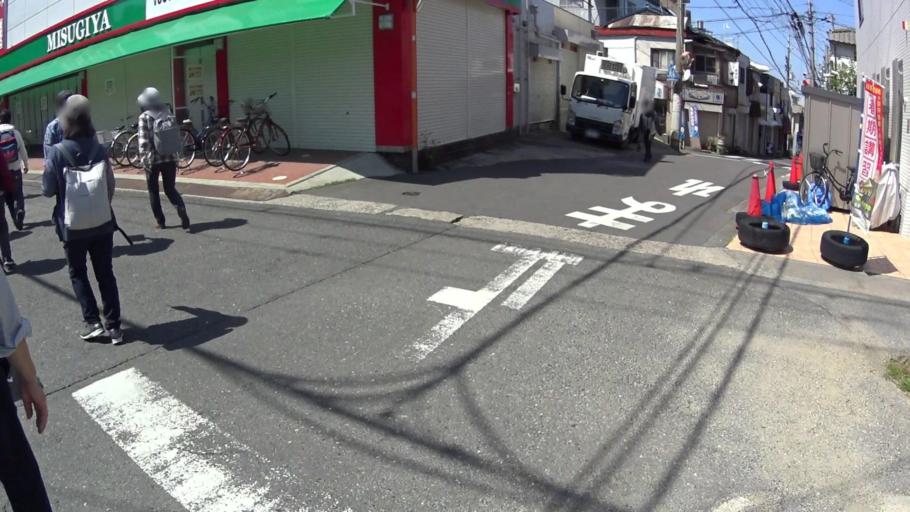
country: JP
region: Osaka
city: Kashihara
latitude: 34.5749
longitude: 135.6150
